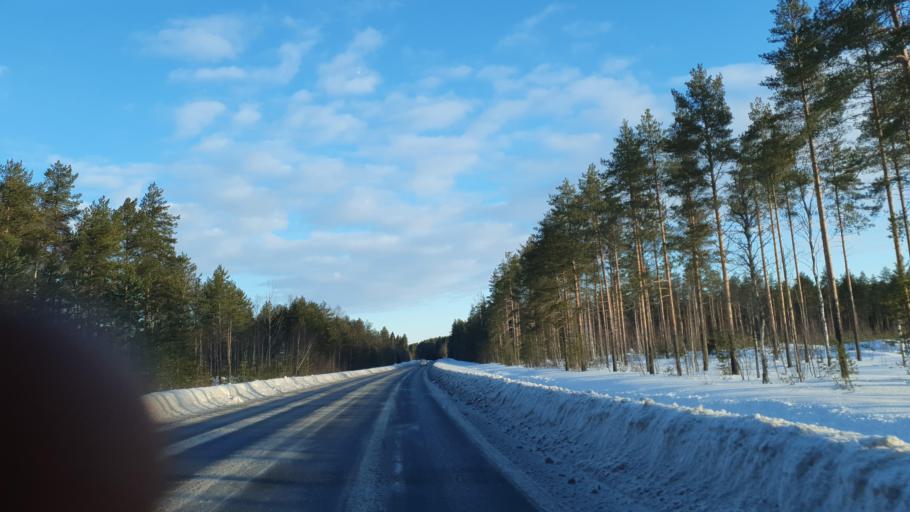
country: FI
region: Northern Ostrobothnia
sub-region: Oulunkaari
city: Utajaervi
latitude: 64.6814
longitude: 26.5357
